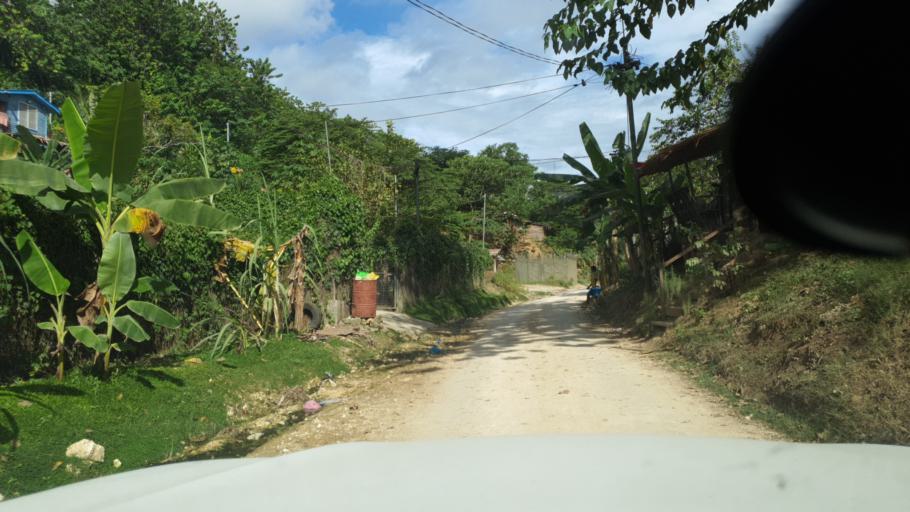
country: SB
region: Guadalcanal
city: Honiara
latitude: -9.4354
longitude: 159.9339
